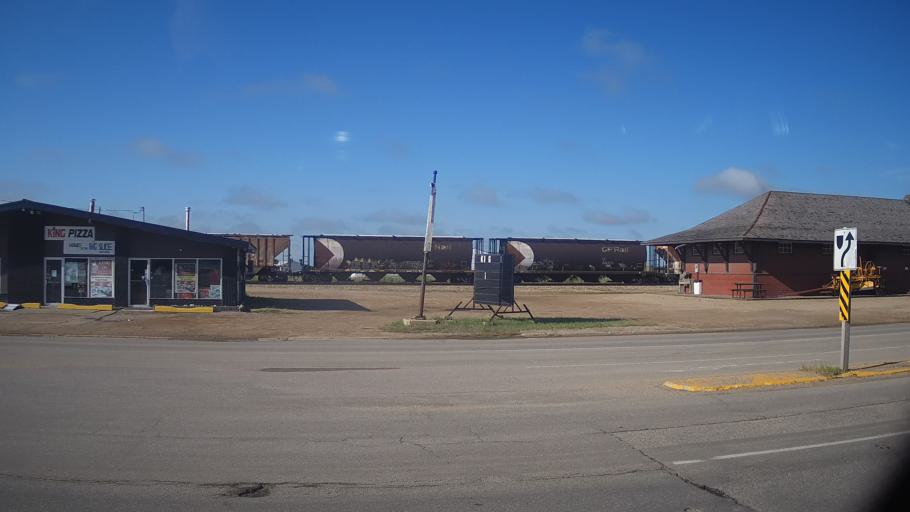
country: CA
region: Saskatchewan
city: Lanigan
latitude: 51.8455
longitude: -105.0340
